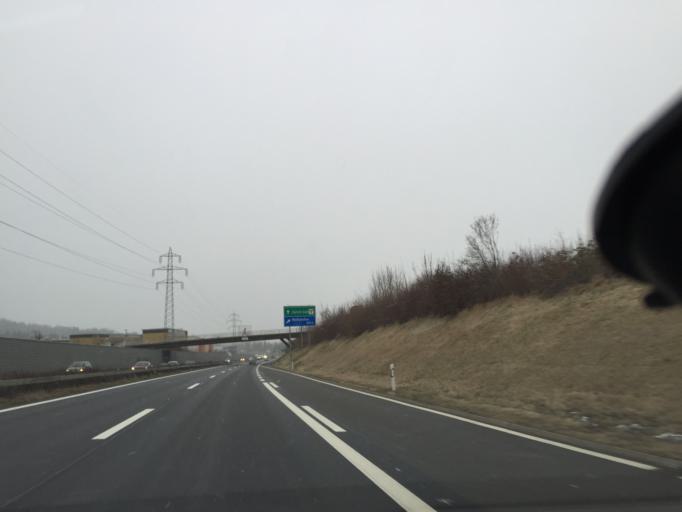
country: CH
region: Zurich
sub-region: Bezirk Horgen
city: Kilchberg / Baechler-Stocken
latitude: 47.3219
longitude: 8.5332
